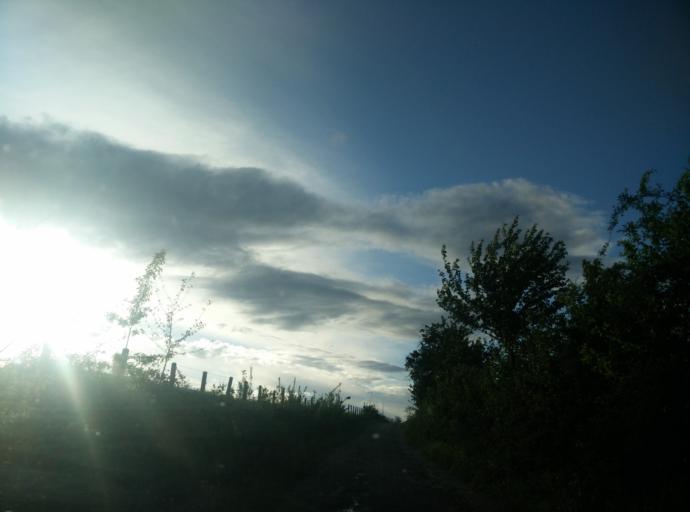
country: BA
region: Brcko
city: Brcko
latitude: 44.7804
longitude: 18.8276
